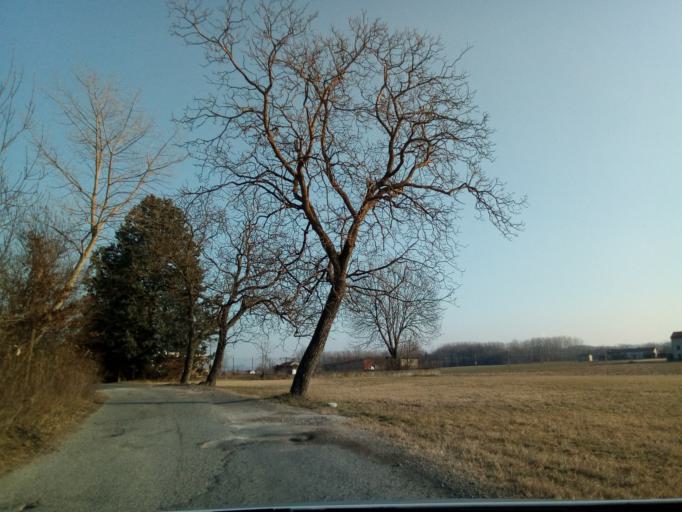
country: IT
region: Piedmont
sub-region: Provincia di Torino
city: Cascinette d'Ivrea
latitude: 45.4686
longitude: 7.9165
